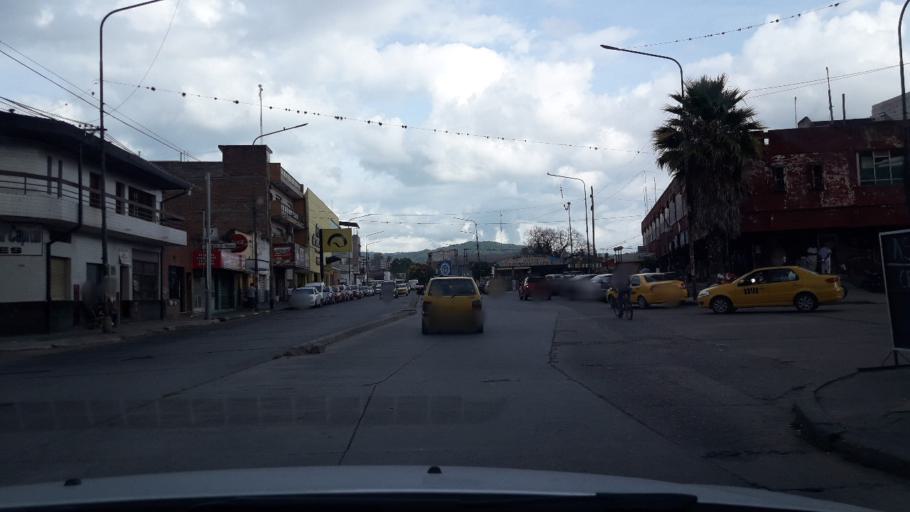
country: AR
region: Jujuy
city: San Salvador de Jujuy
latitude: -24.1939
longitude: -65.2898
